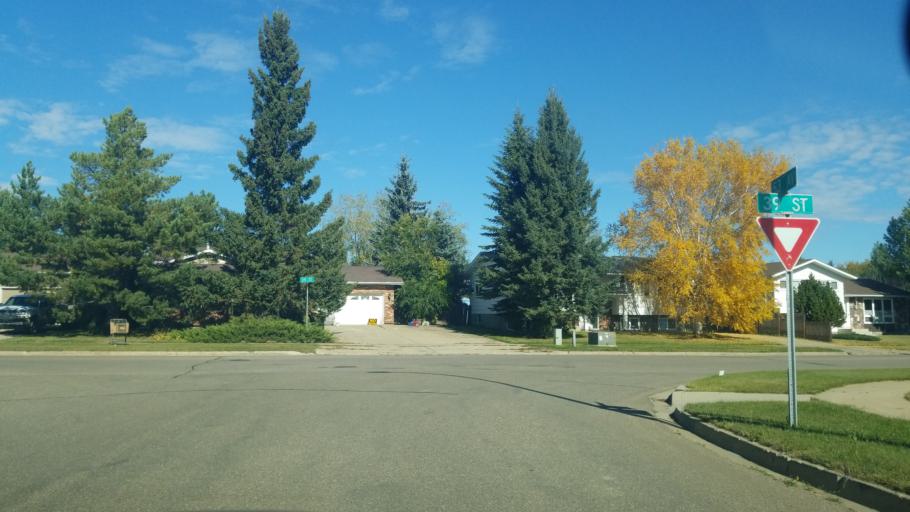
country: CA
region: Saskatchewan
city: Lloydminster
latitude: 53.2728
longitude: -110.0147
